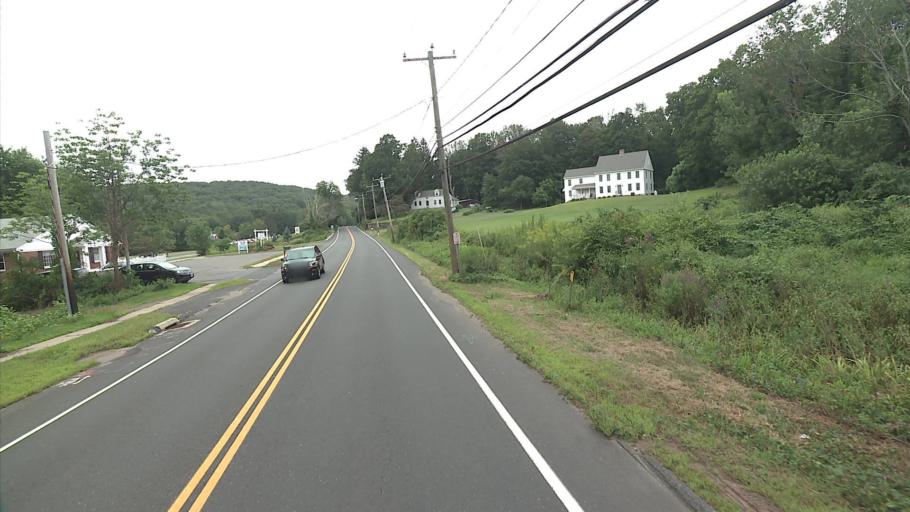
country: US
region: Connecticut
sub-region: Tolland County
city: Tolland
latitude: 41.8738
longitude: -72.3722
